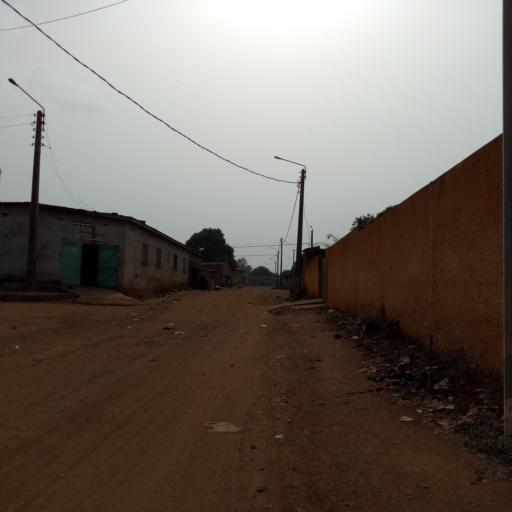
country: CI
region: Vallee du Bandama
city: Bouake
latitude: 7.7029
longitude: -5.0298
